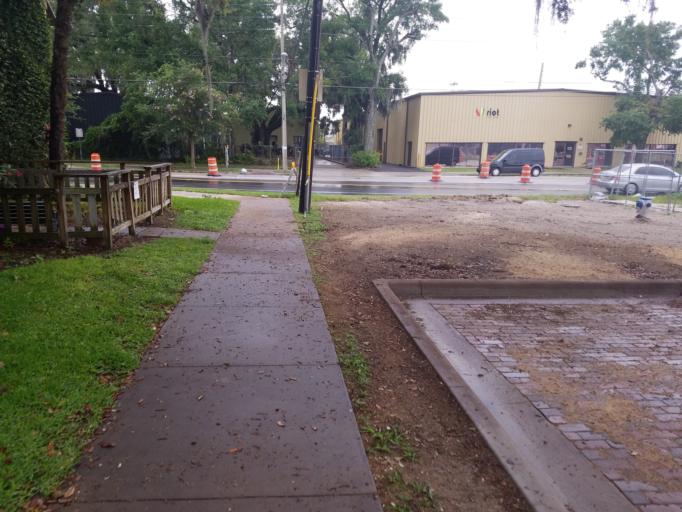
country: US
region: Florida
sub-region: Orange County
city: Orlando
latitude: 28.5645
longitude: -81.3713
